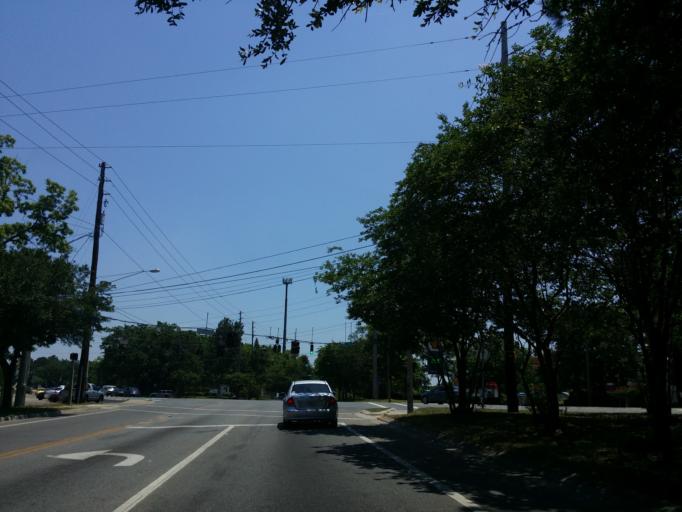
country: US
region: Florida
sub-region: Leon County
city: Tallahassee
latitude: 30.4640
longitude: -84.3007
